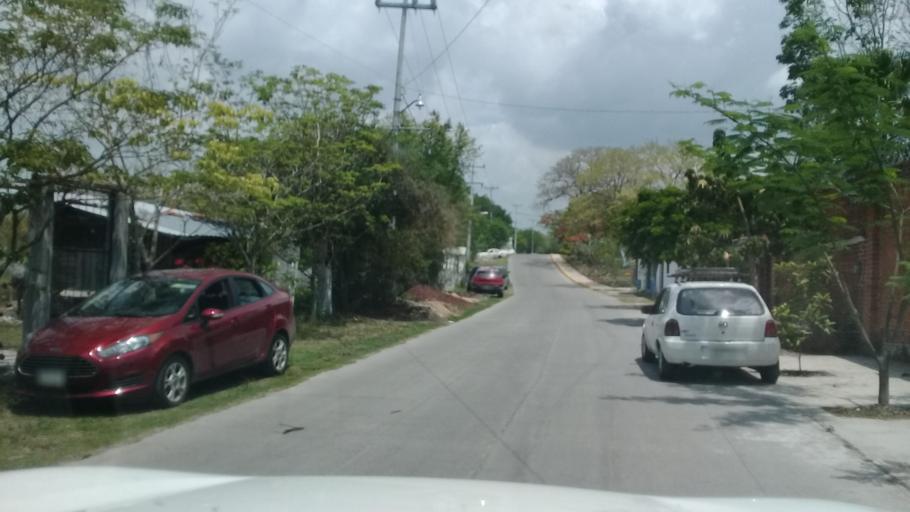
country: MX
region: Veracruz
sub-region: Emiliano Zapata
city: Plan del Rio
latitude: 19.3544
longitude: -96.6478
